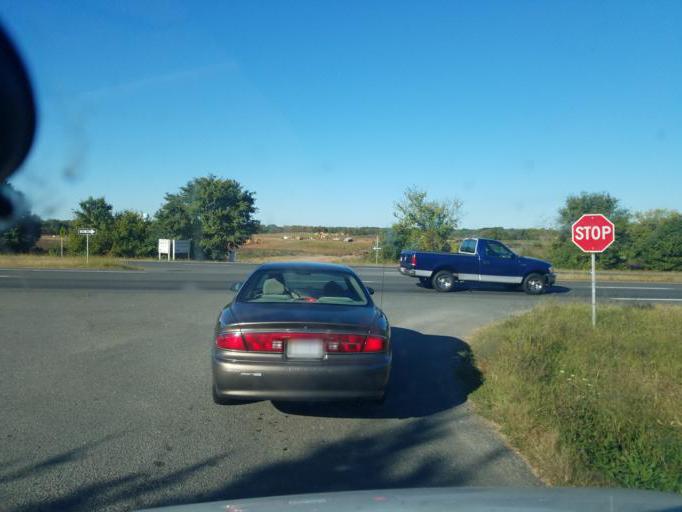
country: US
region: Virginia
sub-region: Fauquier County
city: Bealeton
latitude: 38.5936
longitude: -77.7716
